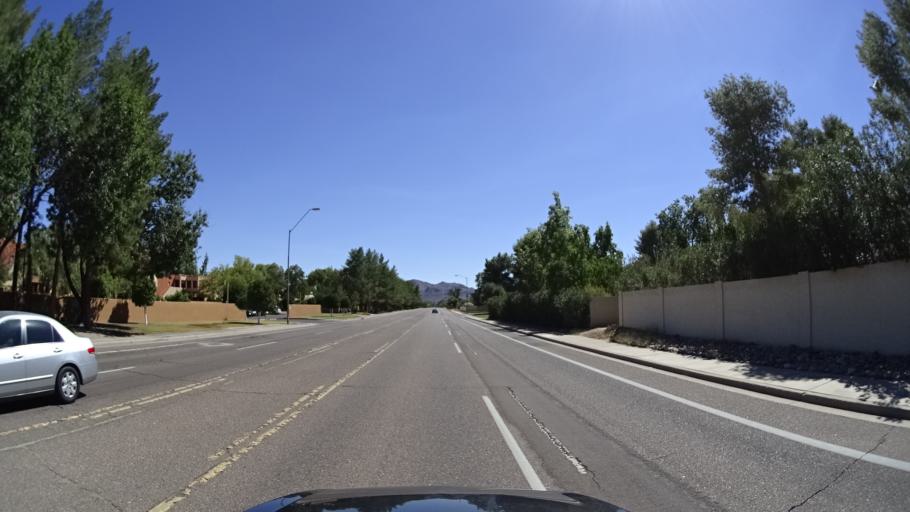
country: US
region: Arizona
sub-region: Maricopa County
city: Paradise Valley
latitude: 33.5867
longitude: -111.9606
